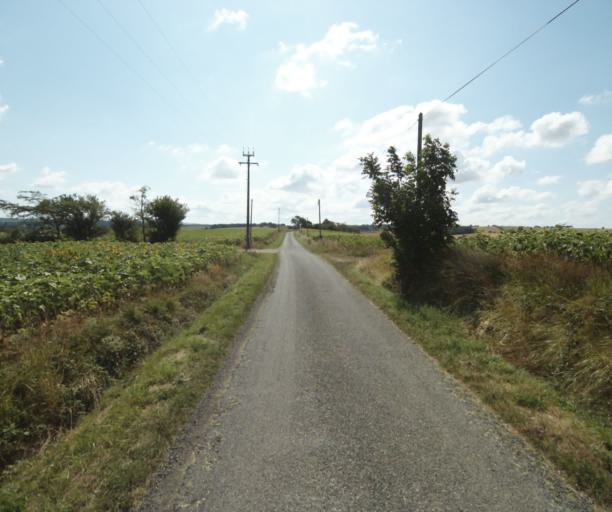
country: FR
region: Midi-Pyrenees
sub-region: Departement de la Haute-Garonne
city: Avignonet-Lauragais
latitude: 43.4421
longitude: 1.7915
